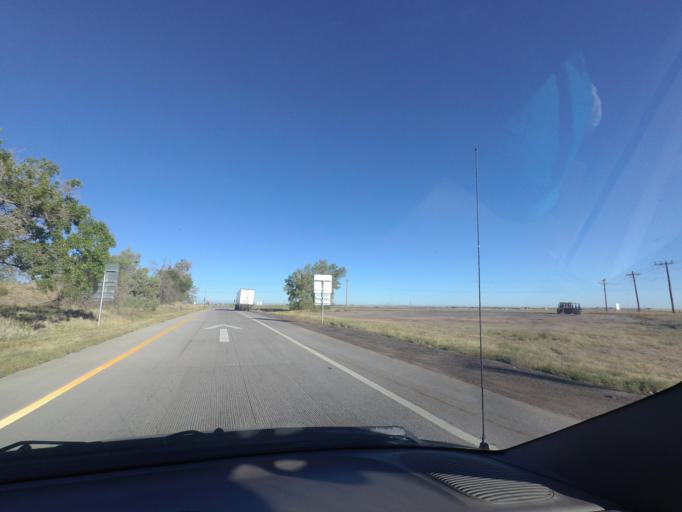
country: US
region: Colorado
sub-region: Adams County
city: Bennett
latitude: 39.7371
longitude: -104.3963
